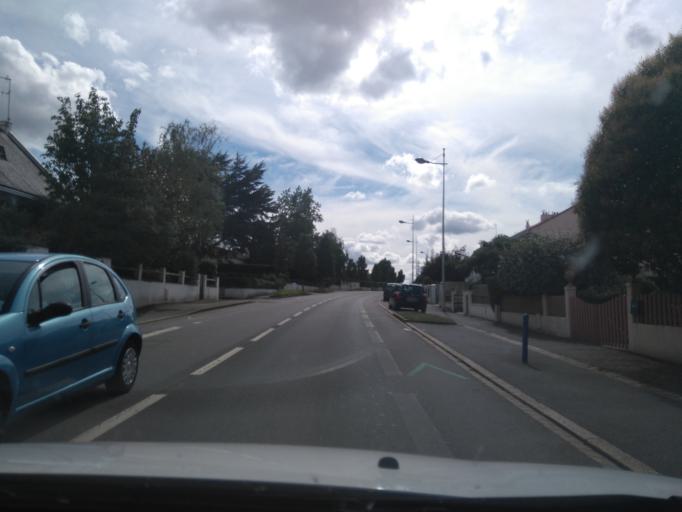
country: FR
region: Pays de la Loire
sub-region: Departement de la Loire-Atlantique
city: Reze
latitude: 47.1728
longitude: -1.5718
